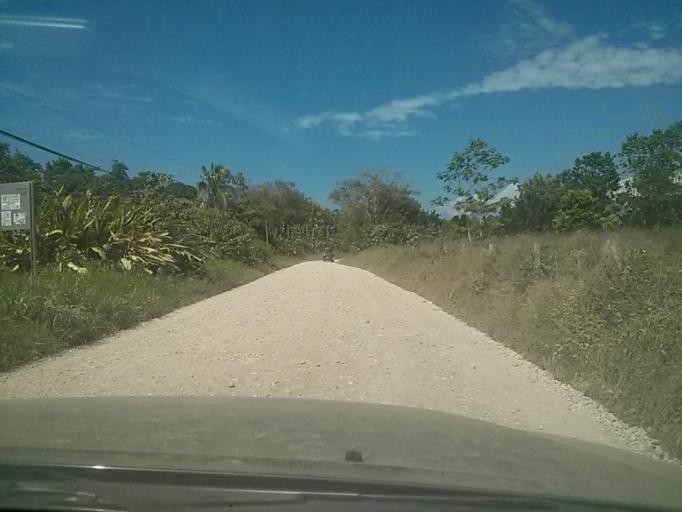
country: CR
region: Puntarenas
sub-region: Canton de Golfito
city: Golfito
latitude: 8.4542
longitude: -83.0488
